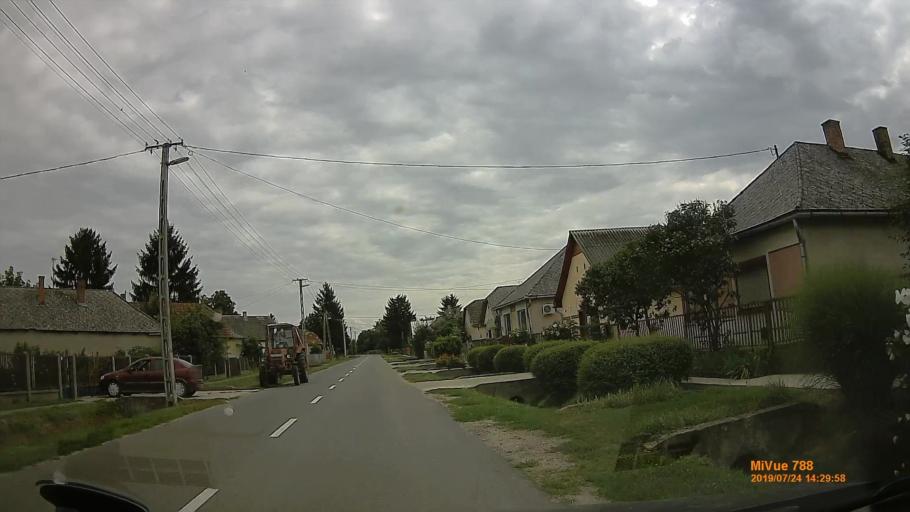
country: HU
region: Szabolcs-Szatmar-Bereg
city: Mandok
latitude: 48.3287
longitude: 22.2653
